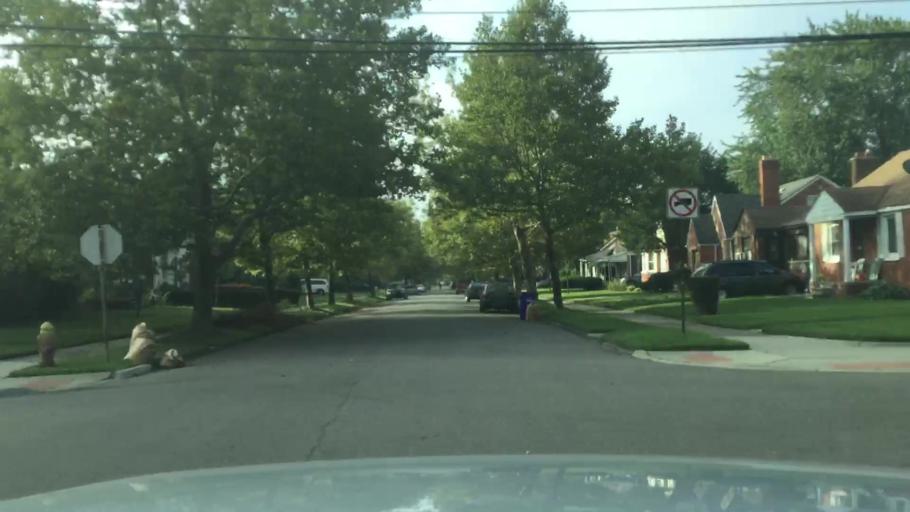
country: US
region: Michigan
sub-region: Wayne County
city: Dearborn
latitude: 42.3637
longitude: -83.1510
